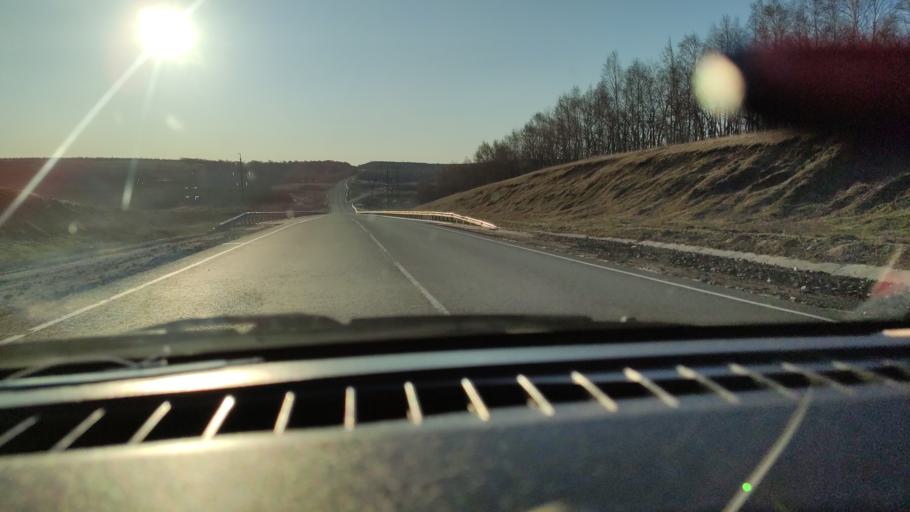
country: RU
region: Saratov
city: Shikhany
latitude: 52.1157
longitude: 47.2934
